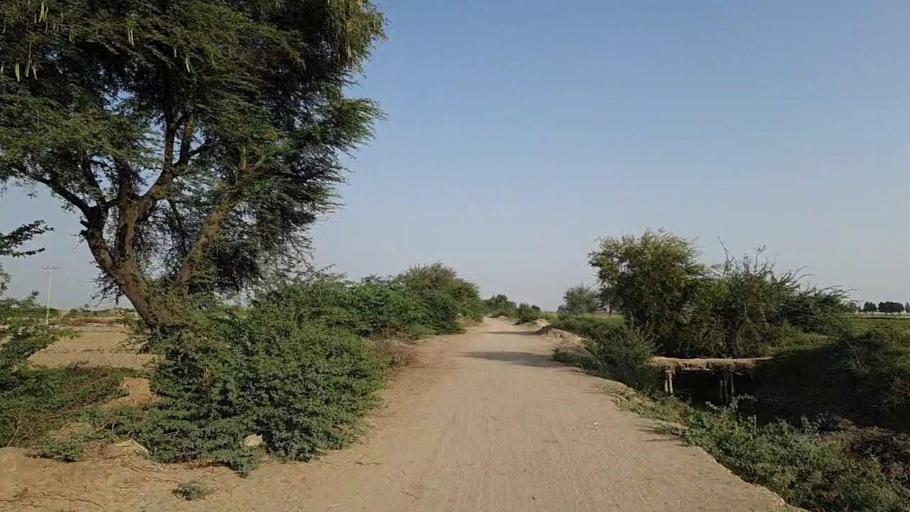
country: PK
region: Sindh
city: Jati
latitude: 24.2635
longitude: 68.1691
